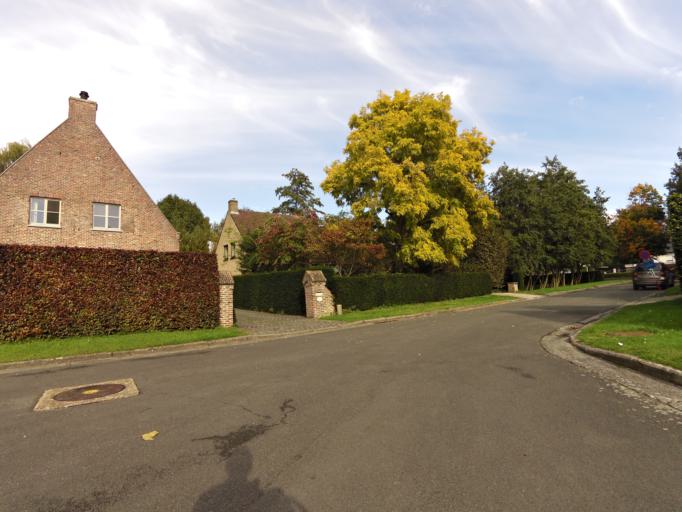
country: BE
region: Flanders
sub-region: Provincie West-Vlaanderen
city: Brugge
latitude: 51.1895
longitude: 3.2158
